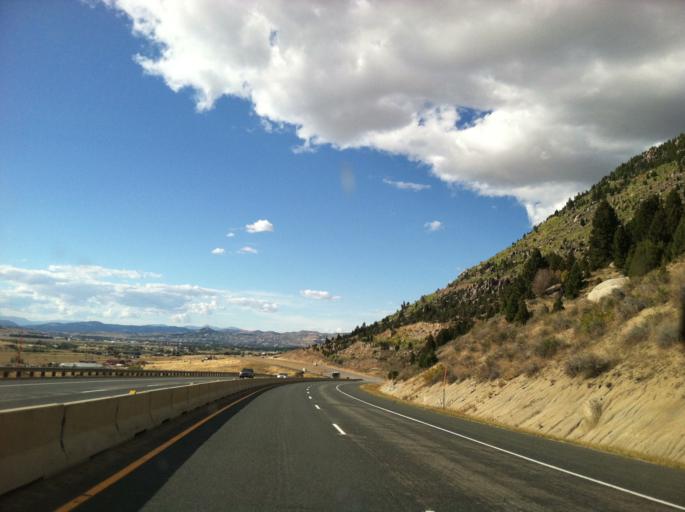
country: US
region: Montana
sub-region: Silver Bow County
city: Butte
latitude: 45.9375
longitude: -112.4559
